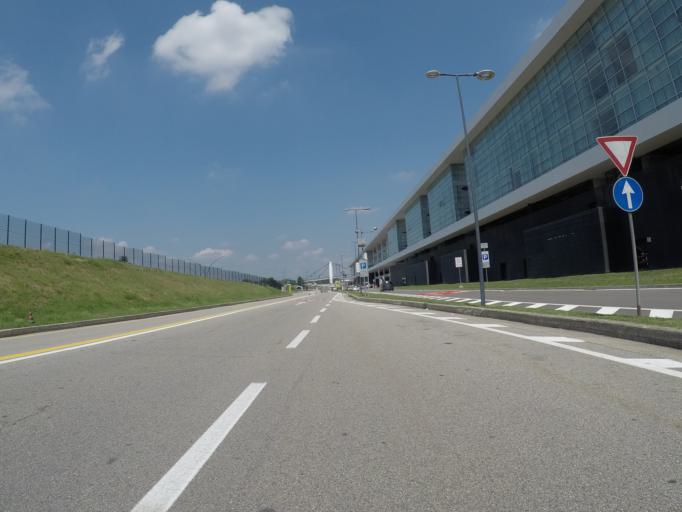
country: IT
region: Lombardy
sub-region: Provincia di Varese
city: Vizzola Ticino
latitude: 45.6254
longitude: 8.7110
